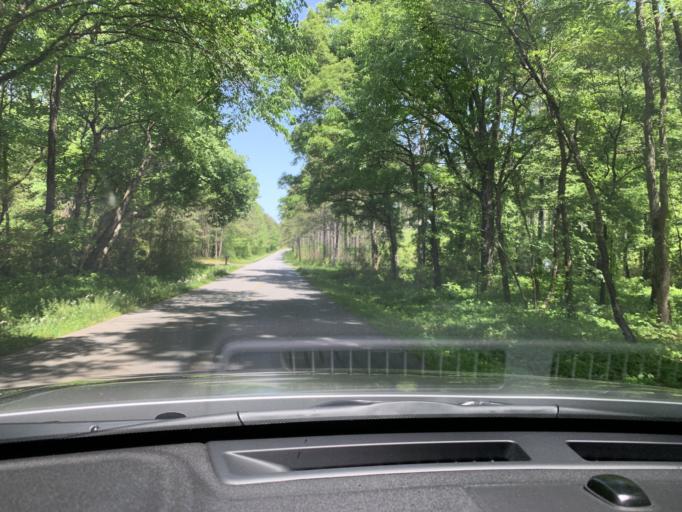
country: US
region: Georgia
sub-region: Polk County
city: Cedartown
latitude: 34.0546
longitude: -85.1844
